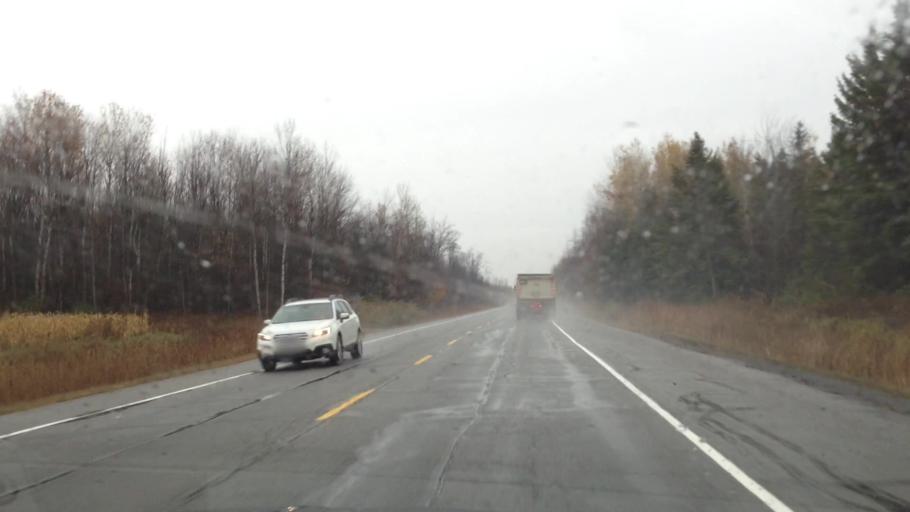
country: CA
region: Ontario
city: Clarence-Rockland
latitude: 45.3628
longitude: -75.3747
